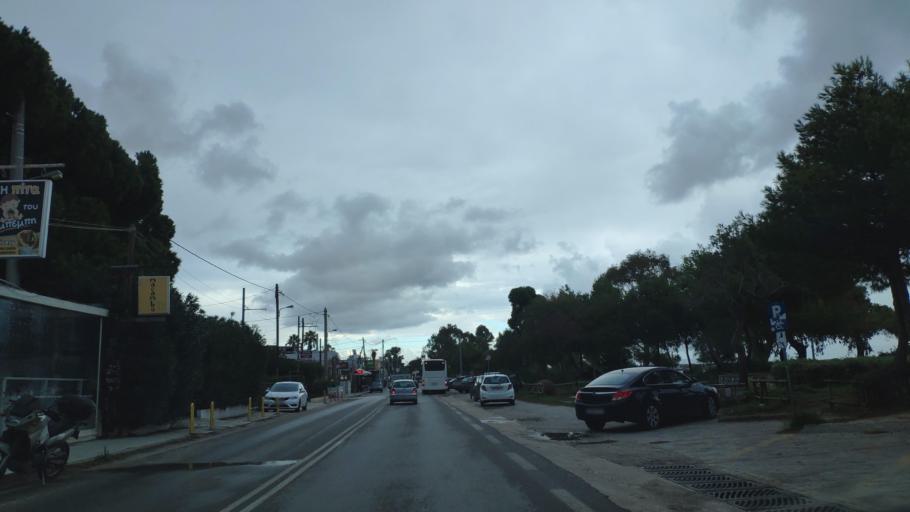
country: GR
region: Attica
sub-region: Nomarchia Anatolikis Attikis
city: Artemida
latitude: 37.9810
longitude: 24.0092
